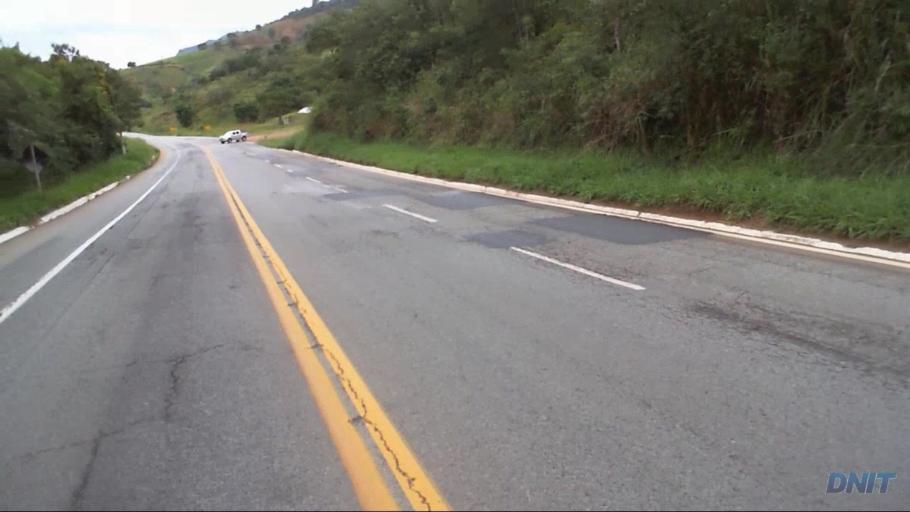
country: BR
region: Minas Gerais
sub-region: Barao De Cocais
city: Barao de Cocais
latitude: -19.8229
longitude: -43.3869
